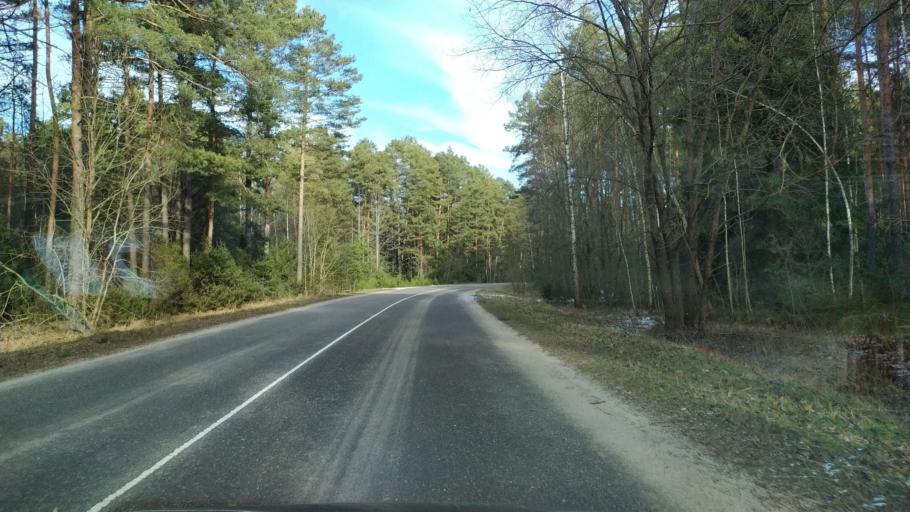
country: BY
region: Brest
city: Pruzhany
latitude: 52.5276
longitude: 24.1778
